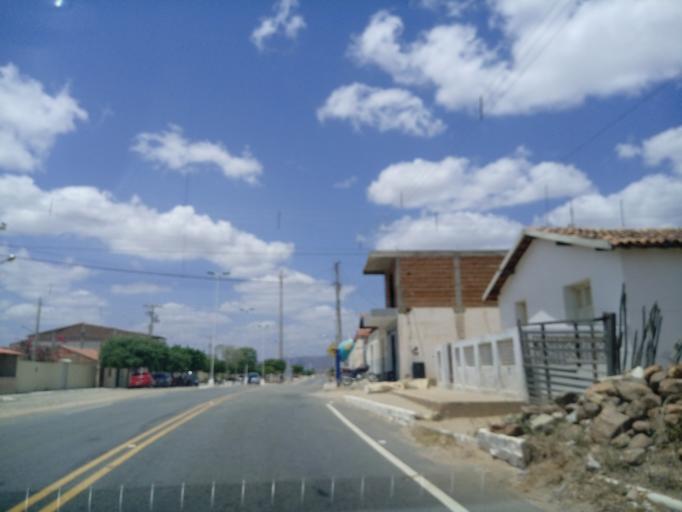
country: BR
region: Paraiba
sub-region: Desterro
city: Desterro
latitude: -7.1178
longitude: -37.0687
